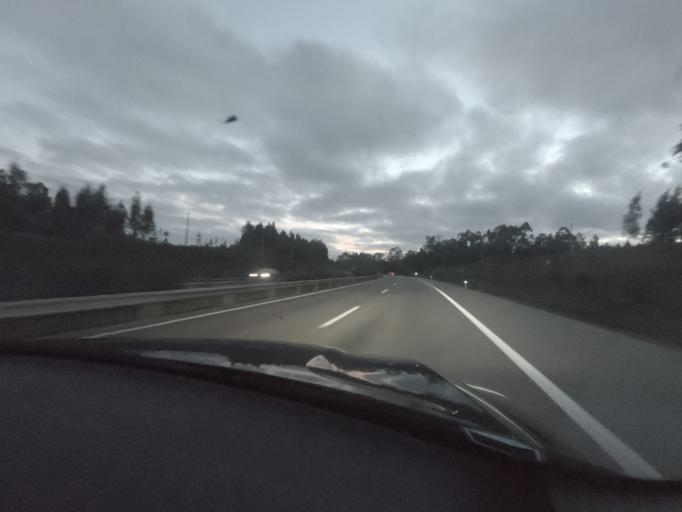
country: PT
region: Leiria
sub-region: Pombal
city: Pombal
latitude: 39.9583
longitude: -8.6663
